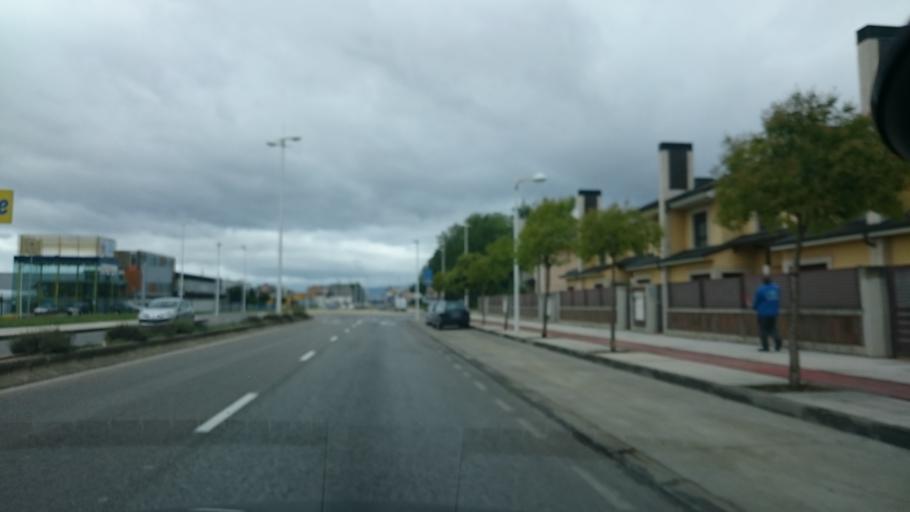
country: ES
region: Castille and Leon
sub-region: Provincia de Leon
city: Ponferrada
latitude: 42.5549
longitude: -6.6128
